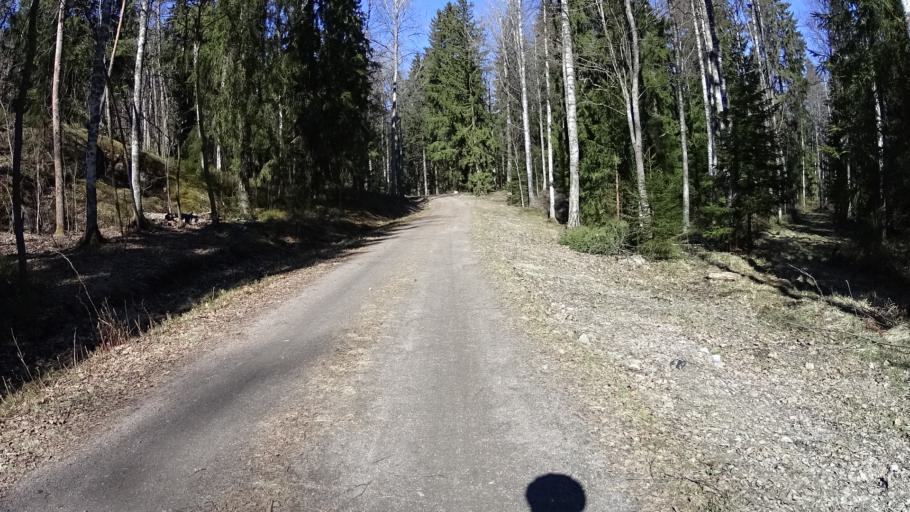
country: FI
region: Uusimaa
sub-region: Helsinki
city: Espoo
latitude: 60.2341
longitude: 24.6406
